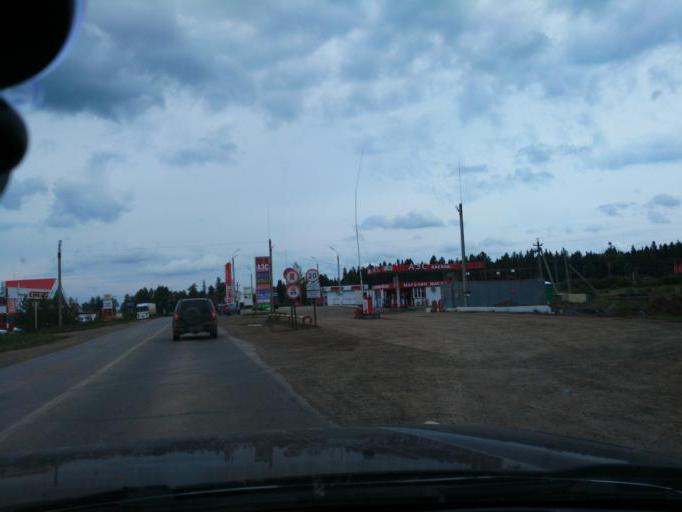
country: RU
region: Perm
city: Chernushka
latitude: 56.5327
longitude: 56.0903
